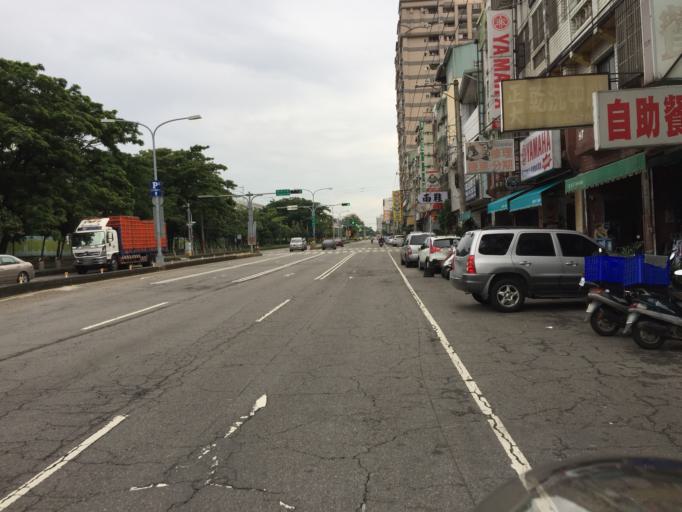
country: TW
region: Taiwan
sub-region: Taichung City
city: Taichung
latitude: 24.1525
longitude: 120.6986
